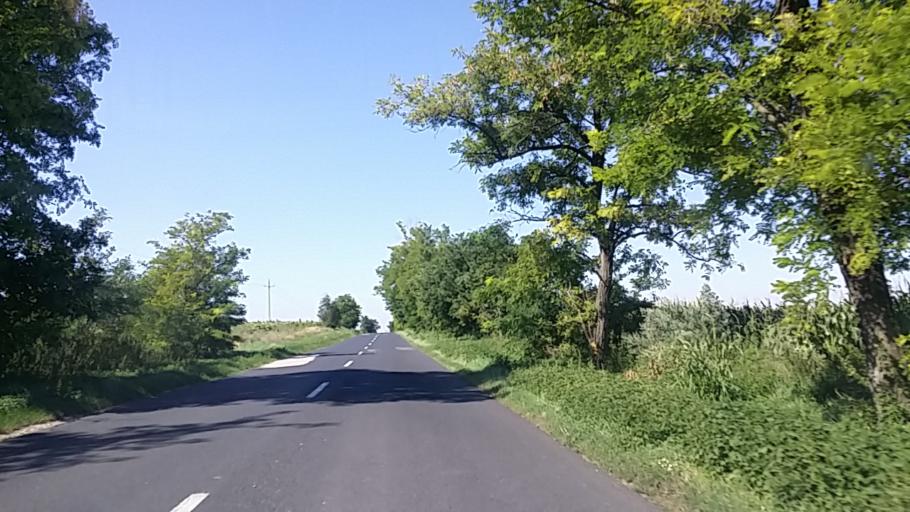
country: HU
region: Fejer
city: Sarbogard
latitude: 46.8848
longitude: 18.6889
